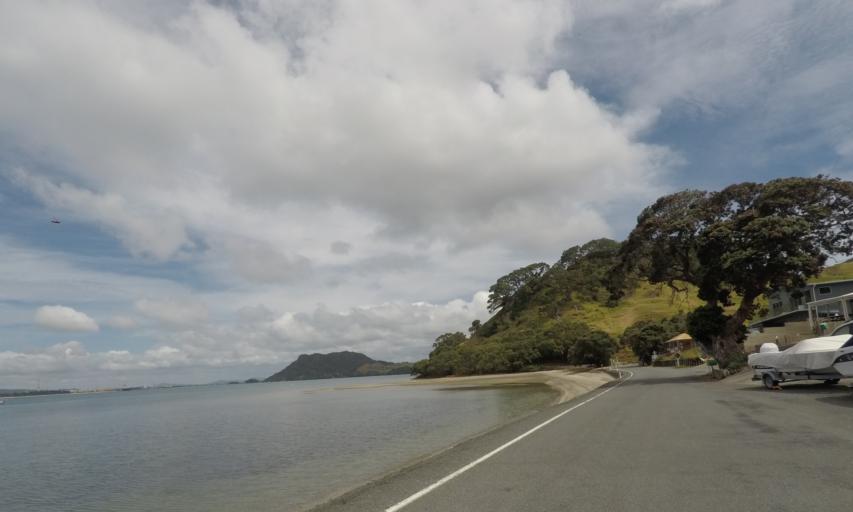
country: NZ
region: Northland
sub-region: Whangarei
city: Ruakaka
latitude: -35.8416
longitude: 174.5363
